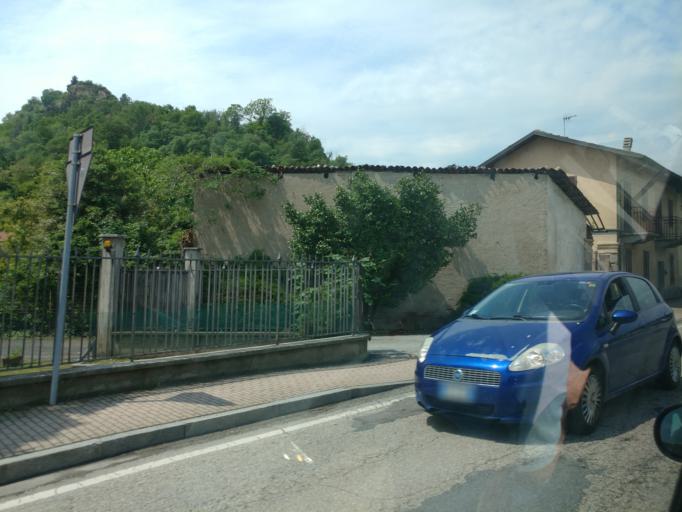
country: IT
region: Piedmont
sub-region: Provincia di Torino
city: Cavour
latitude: 44.7832
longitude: 7.3805
